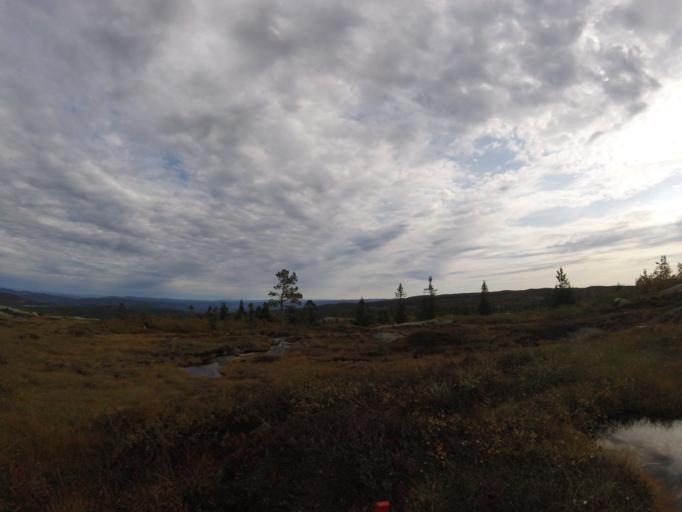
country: NO
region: Buskerud
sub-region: Rollag
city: Rollag
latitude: 59.8081
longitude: 9.3177
